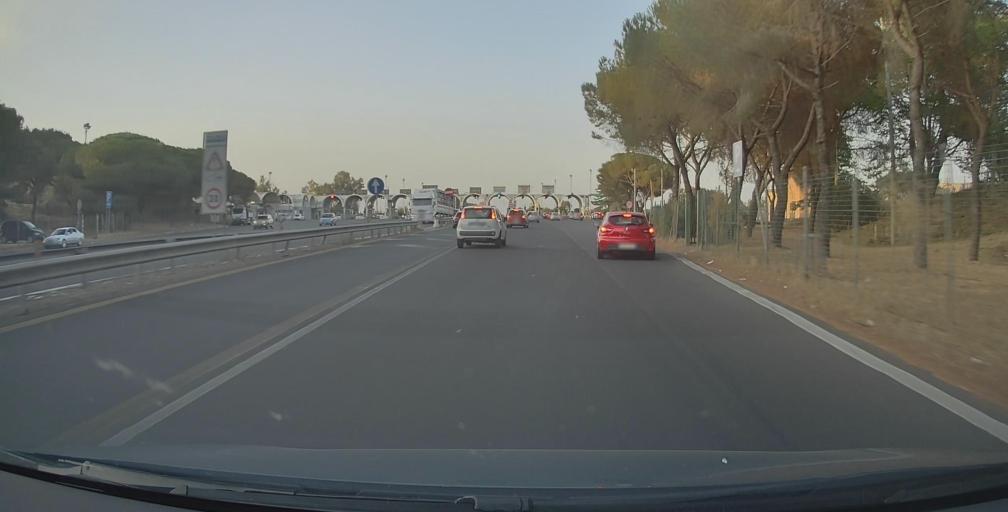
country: IT
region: Sicily
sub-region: Catania
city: San Gregorio di Catania
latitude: 37.5657
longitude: 15.1020
